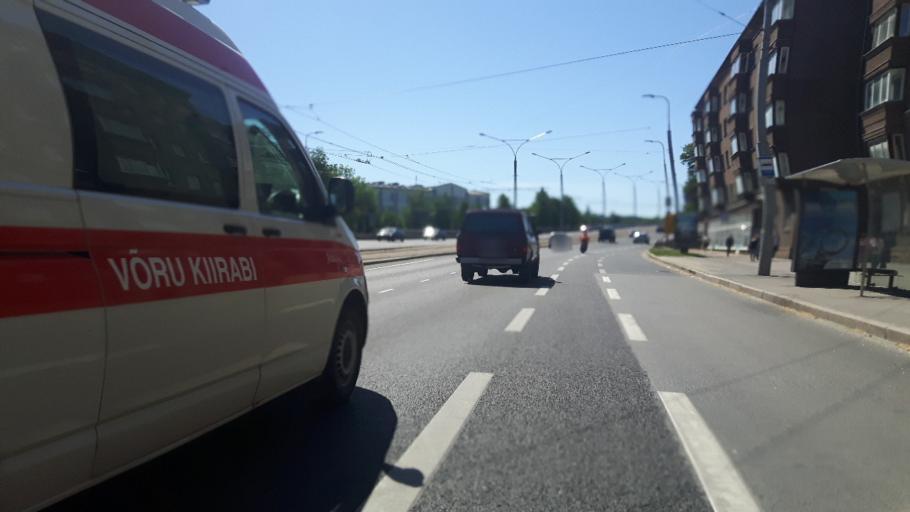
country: EE
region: Harju
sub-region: Tallinna linn
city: Tallinn
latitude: 59.4227
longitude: 24.7423
